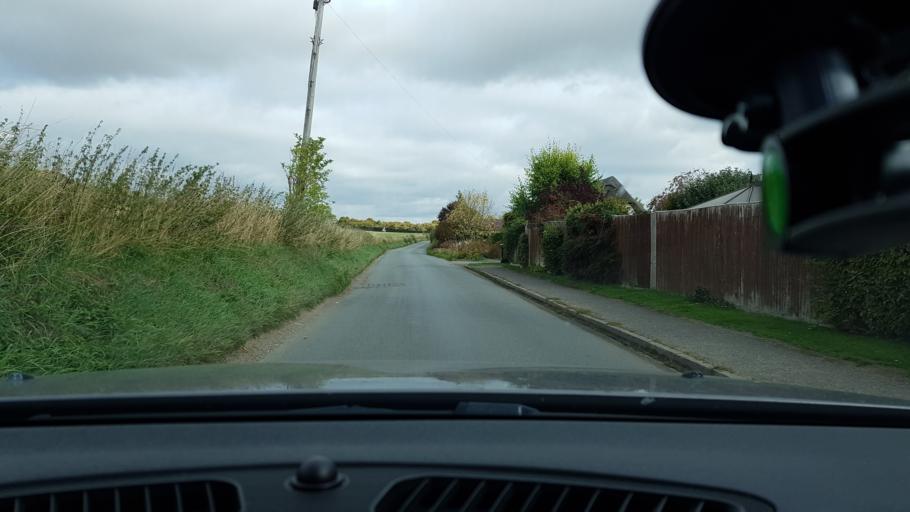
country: GB
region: England
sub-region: Wiltshire
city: Great Bedwyn
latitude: 51.3825
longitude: -1.6006
